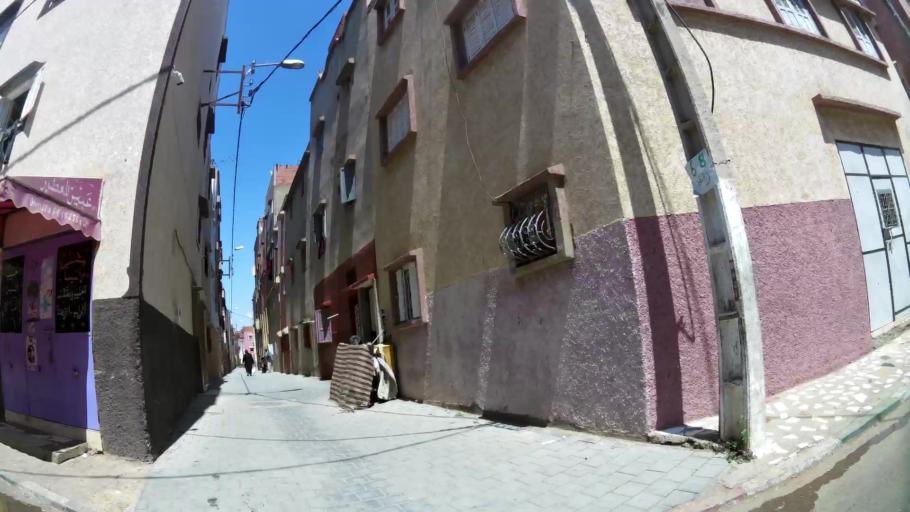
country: MA
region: Gharb-Chrarda-Beni Hssen
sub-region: Kenitra Province
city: Kenitra
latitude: 34.2503
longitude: -6.5546
